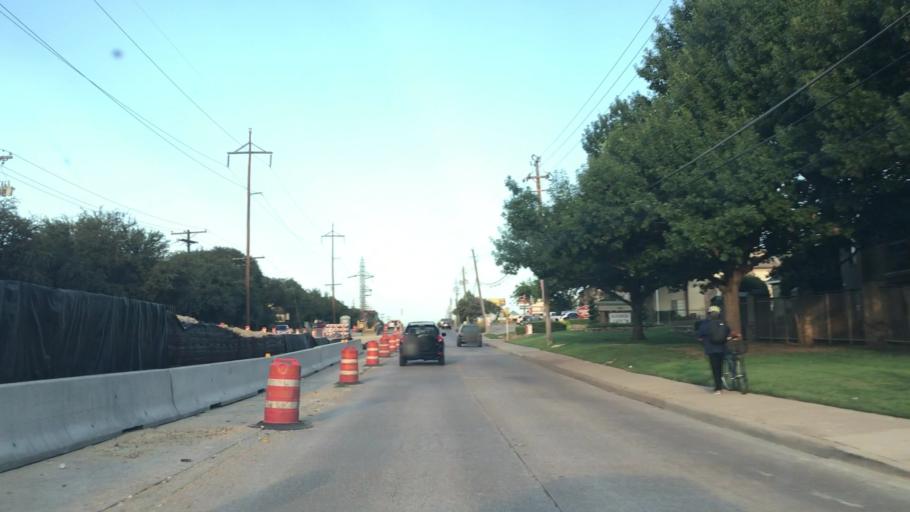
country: US
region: Texas
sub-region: Dallas County
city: Richardson
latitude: 32.9400
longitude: -96.7561
